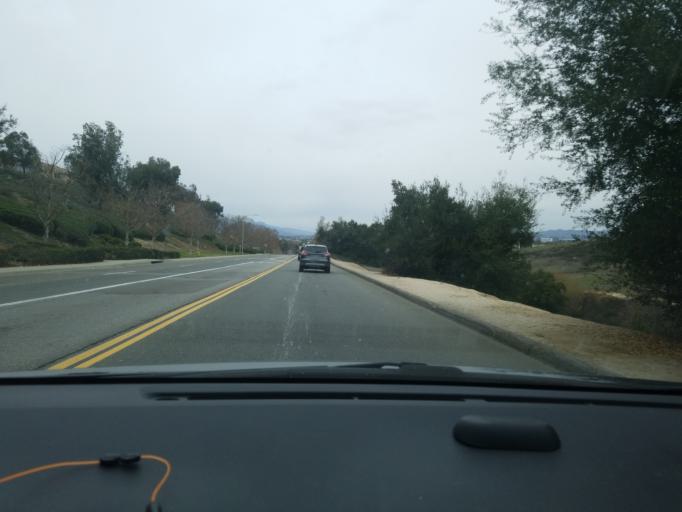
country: US
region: California
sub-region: Riverside County
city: Temecula
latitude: 33.4986
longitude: -117.1429
